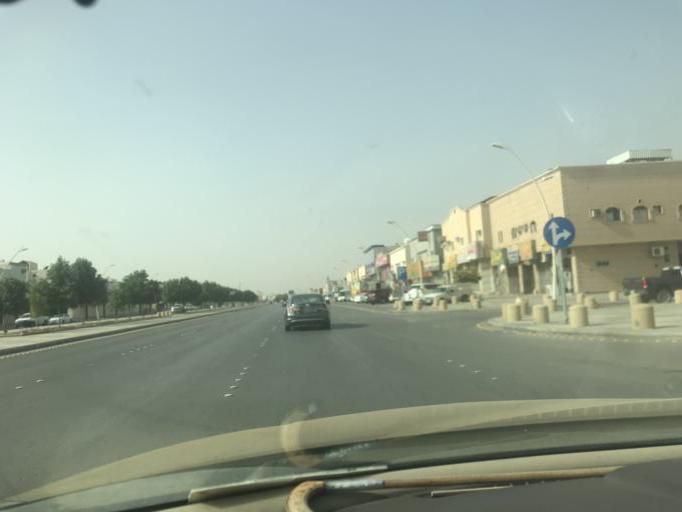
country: SA
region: Ar Riyad
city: Riyadh
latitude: 24.6792
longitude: 46.8001
